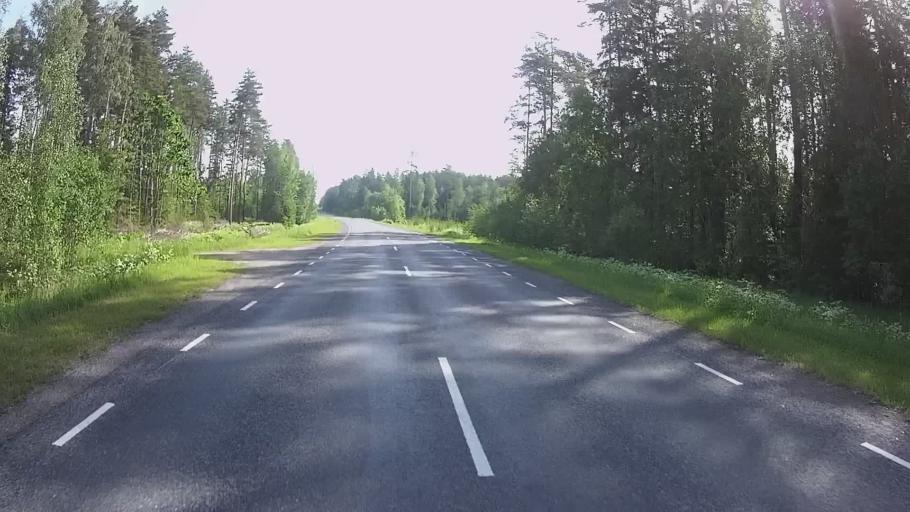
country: EE
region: Valgamaa
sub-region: Torva linn
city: Torva
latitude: 58.0581
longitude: 26.0126
